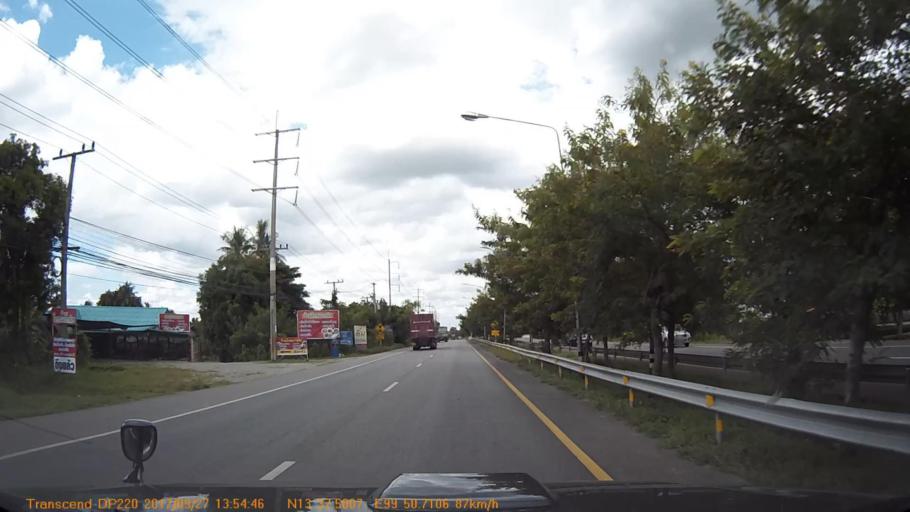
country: TH
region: Ratchaburi
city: Photharam
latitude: 13.6264
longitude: 99.8452
